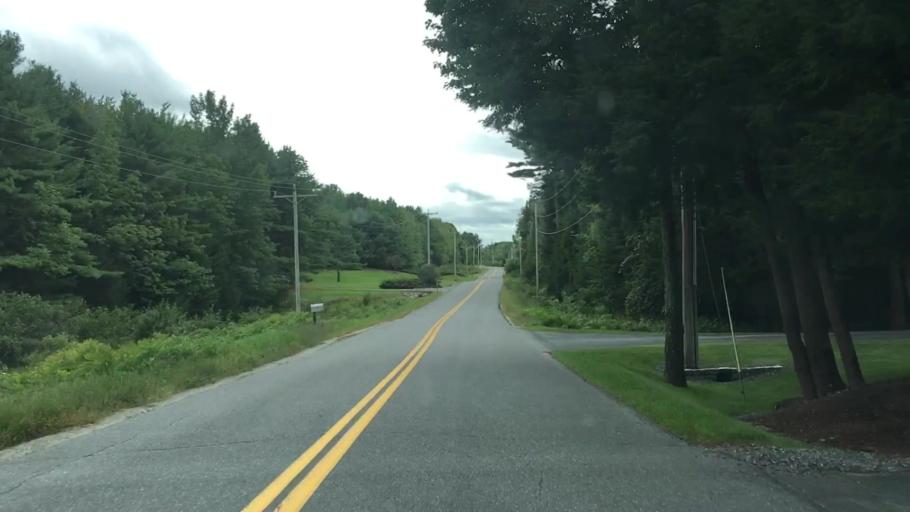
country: US
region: Maine
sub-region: Kennebec County
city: Hallowell
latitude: 44.2690
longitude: -69.8131
